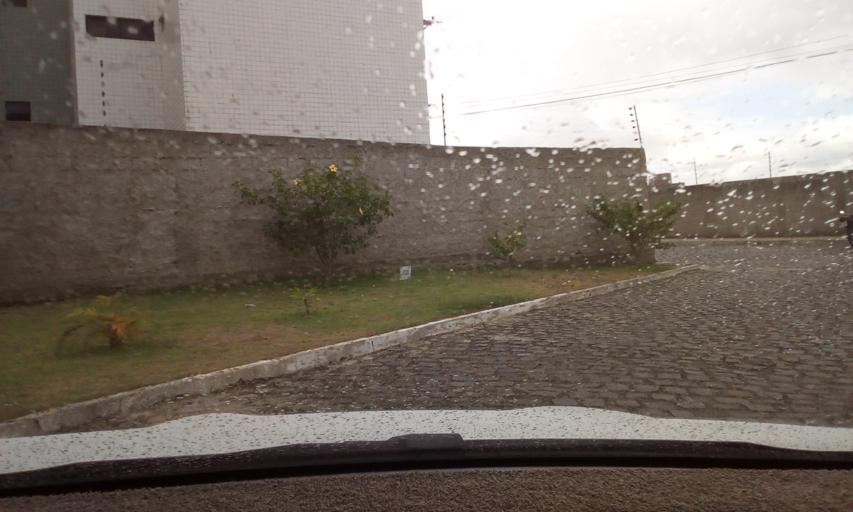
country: BR
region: Paraiba
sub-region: Joao Pessoa
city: Joao Pessoa
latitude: -7.1442
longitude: -34.8333
